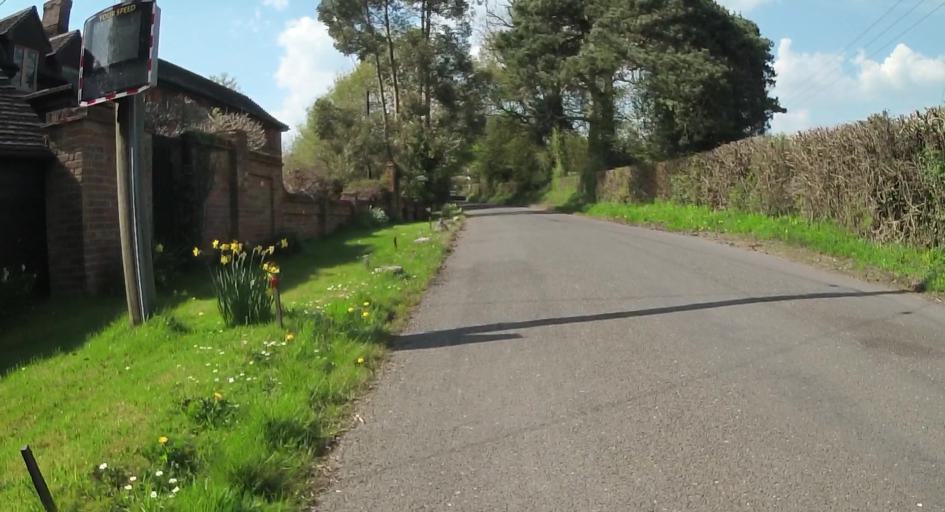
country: GB
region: England
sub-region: Hampshire
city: Tadley
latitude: 51.3514
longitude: -1.0956
